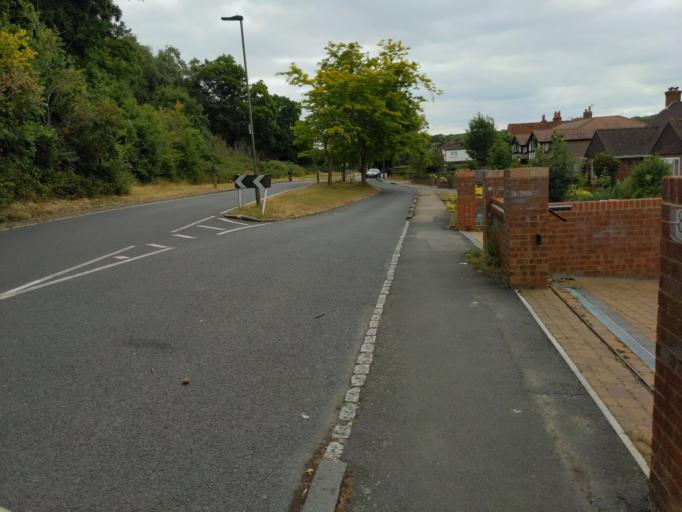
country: GB
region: England
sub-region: Greater London
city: West Wickham
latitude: 51.3695
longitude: 0.0047
